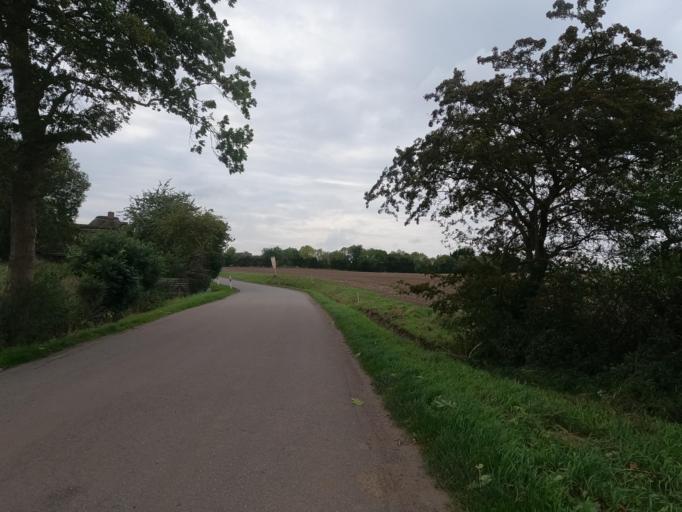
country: DE
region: Schleswig-Holstein
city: Neukirchen
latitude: 54.3245
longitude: 11.0451
